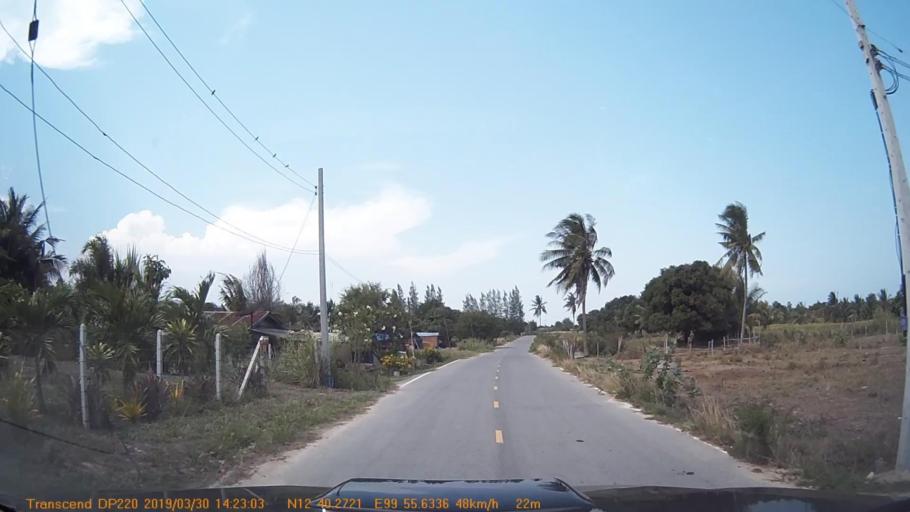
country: TH
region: Prachuap Khiri Khan
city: Hua Hin
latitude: 12.6715
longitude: 99.9273
